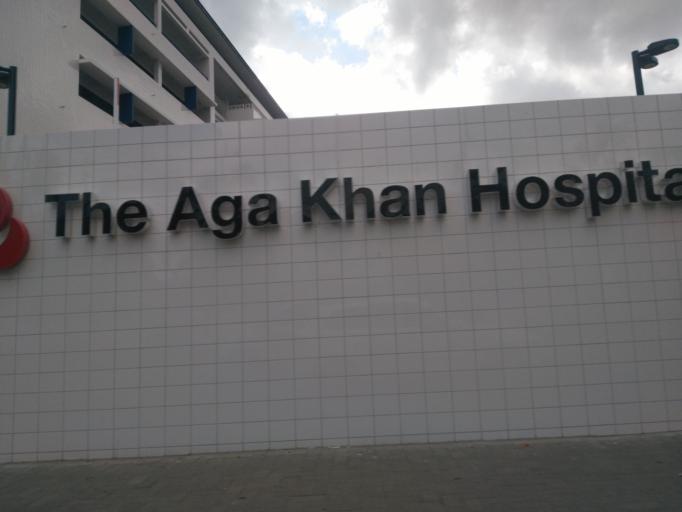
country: TZ
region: Dar es Salaam
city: Dar es Salaam
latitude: -6.8034
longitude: 39.2874
